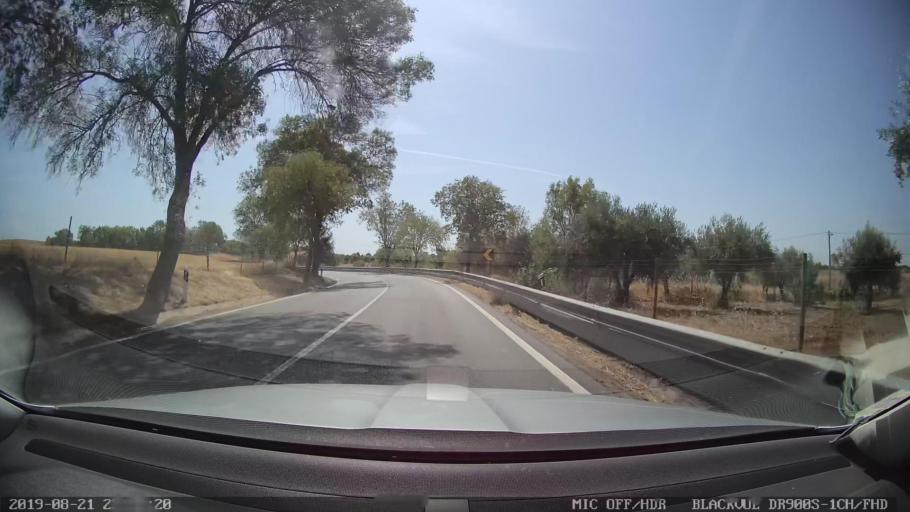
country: PT
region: Castelo Branco
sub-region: Idanha-A-Nova
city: Idanha-a-Nova
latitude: 39.8462
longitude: -7.2798
